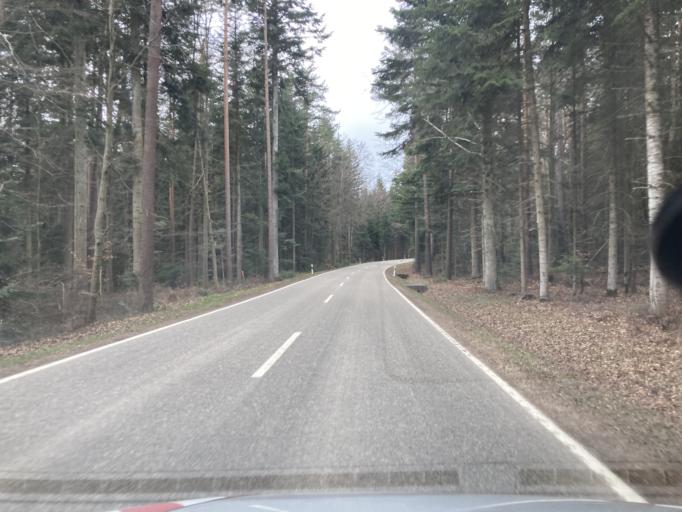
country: DE
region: Baden-Wuerttemberg
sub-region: Karlsruhe Region
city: Neuweiler
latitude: 48.6672
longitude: 8.6228
